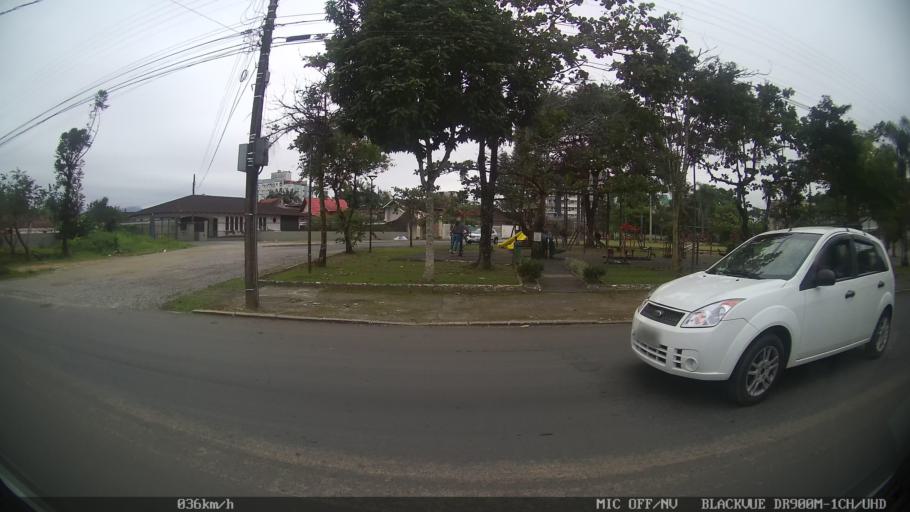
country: BR
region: Santa Catarina
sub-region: Joinville
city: Joinville
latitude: -26.2738
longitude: -48.8459
